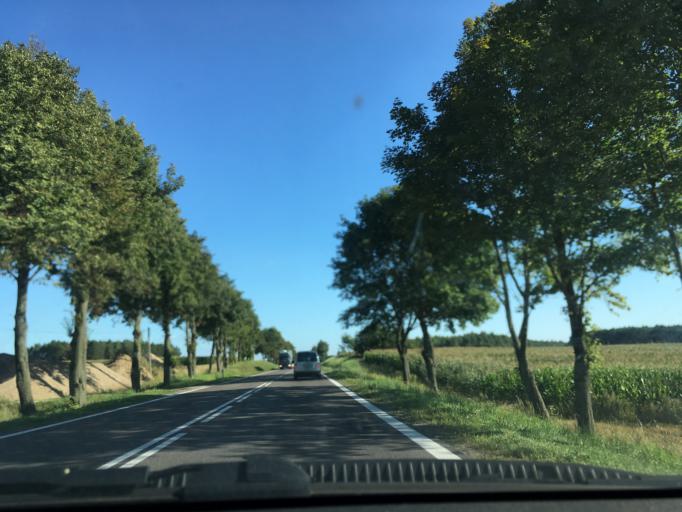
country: PL
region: Podlasie
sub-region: Powiat sokolski
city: Janow
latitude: 53.4279
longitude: 23.1053
